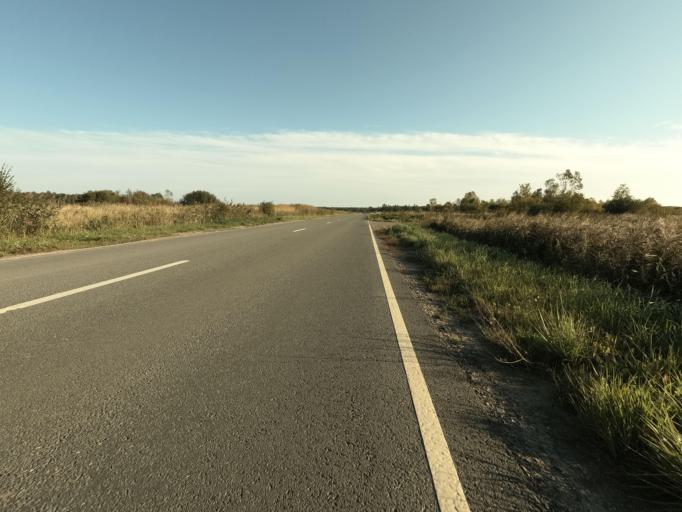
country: RU
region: St.-Petersburg
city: Sapernyy
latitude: 59.7346
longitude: 30.6563
